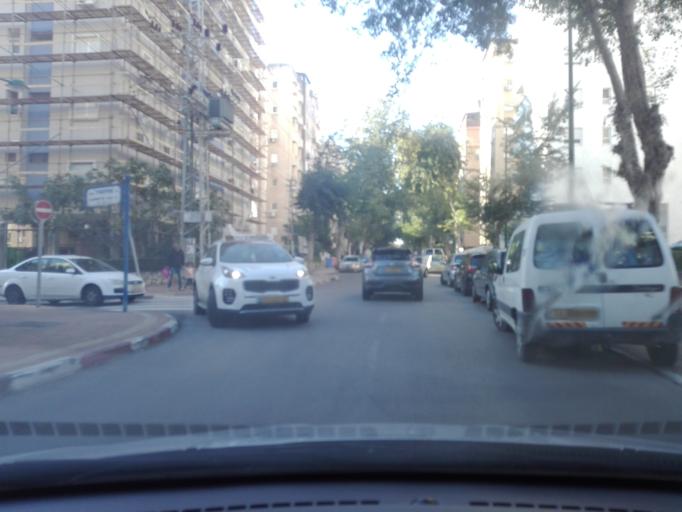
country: IL
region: Central District
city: Netanya
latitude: 32.3214
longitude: 34.8515
